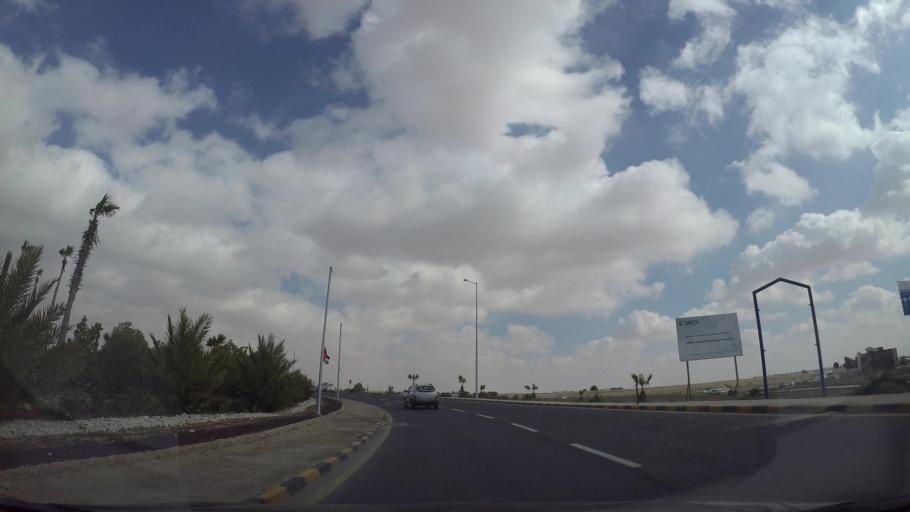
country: JO
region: Amman
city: Al Jizah
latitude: 31.7202
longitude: 35.9678
